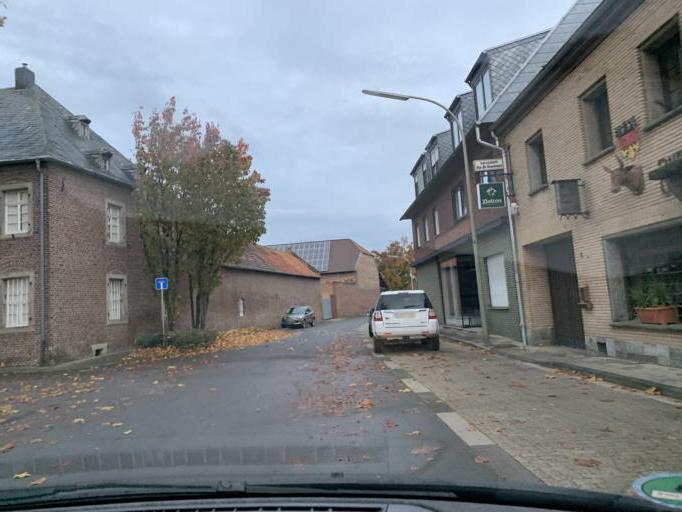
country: DE
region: North Rhine-Westphalia
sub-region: Regierungsbezirk Koln
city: Titz
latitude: 51.0481
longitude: 6.4057
